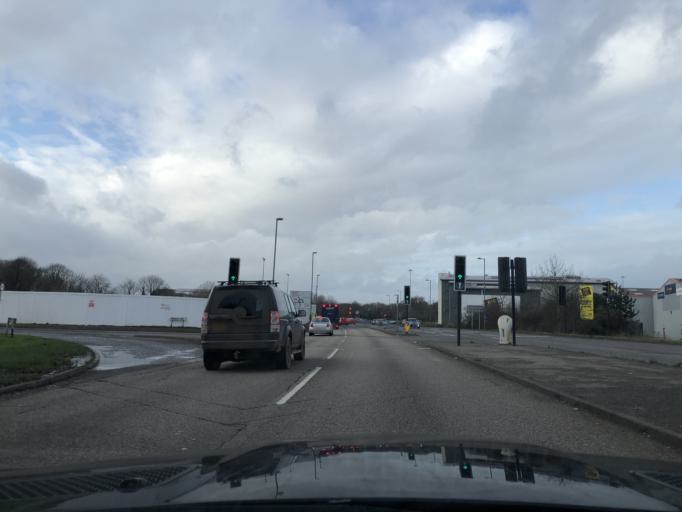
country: GB
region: England
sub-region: Bracknell Forest
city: Sandhurst
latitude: 51.3308
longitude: -0.7722
